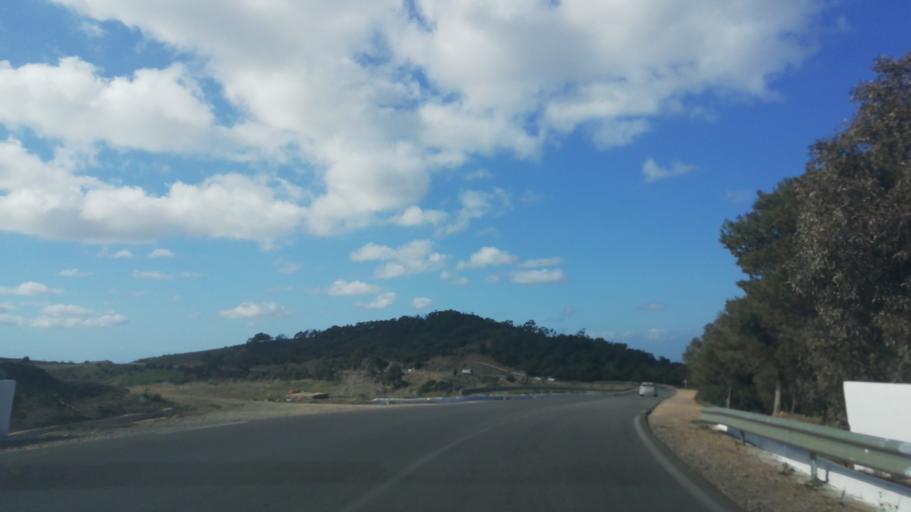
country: DZ
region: Relizane
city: Relizane
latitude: 36.0901
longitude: 0.4693
